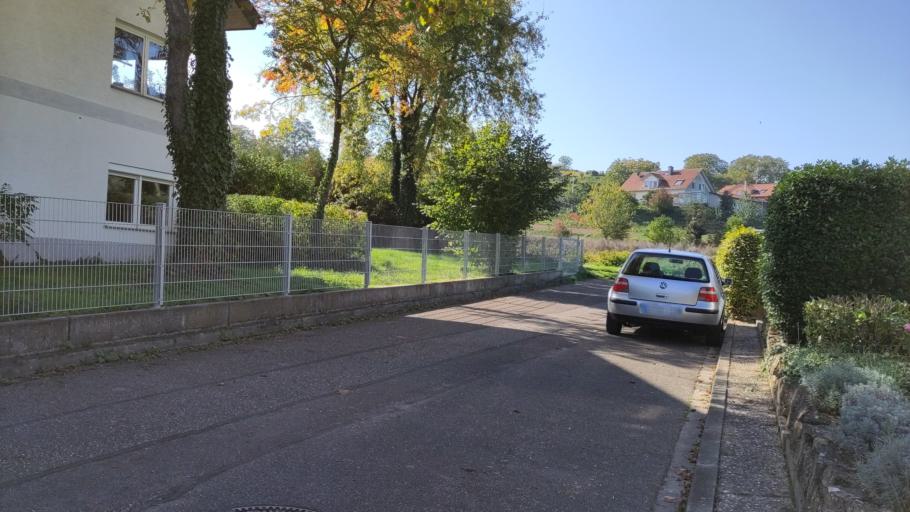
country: DE
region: Baden-Wuerttemberg
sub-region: Freiburg Region
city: Bahlingen
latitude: 48.1175
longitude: 7.7277
